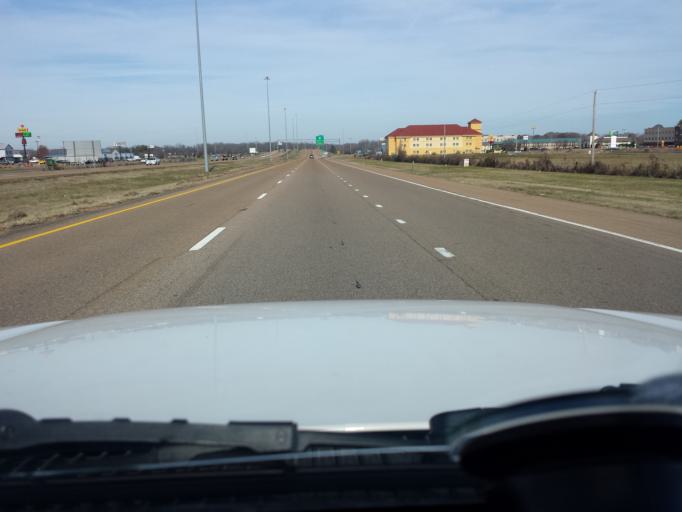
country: US
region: Mississippi
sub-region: Madison County
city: Canton
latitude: 32.5984
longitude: -90.0692
